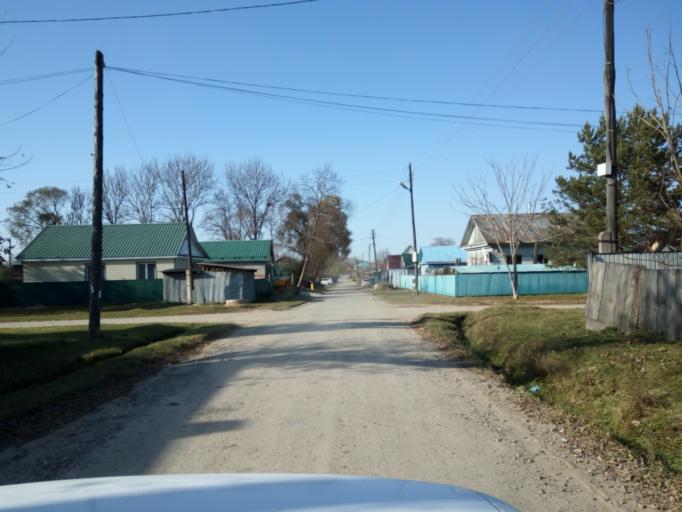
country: RU
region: Primorskiy
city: Dal'nerechensk
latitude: 45.9225
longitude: 133.7339
